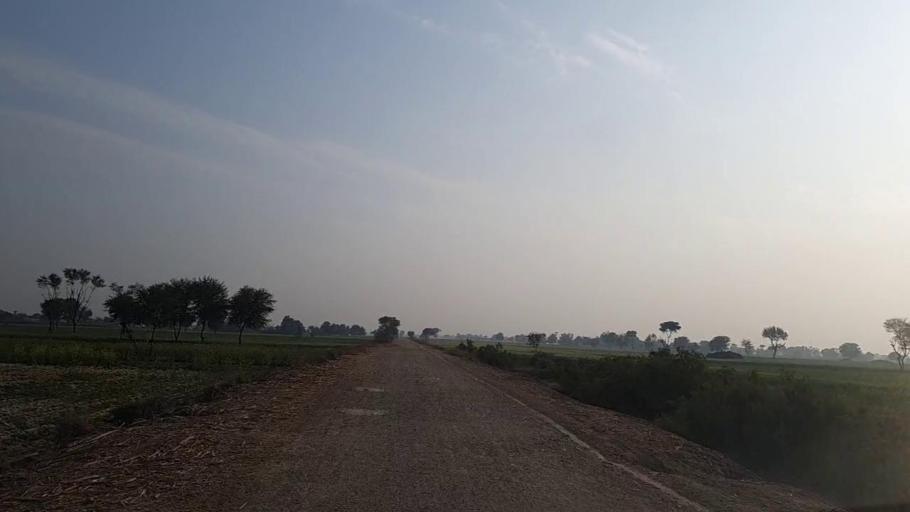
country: PK
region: Sindh
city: Jam Sahib
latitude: 26.3155
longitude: 68.5336
